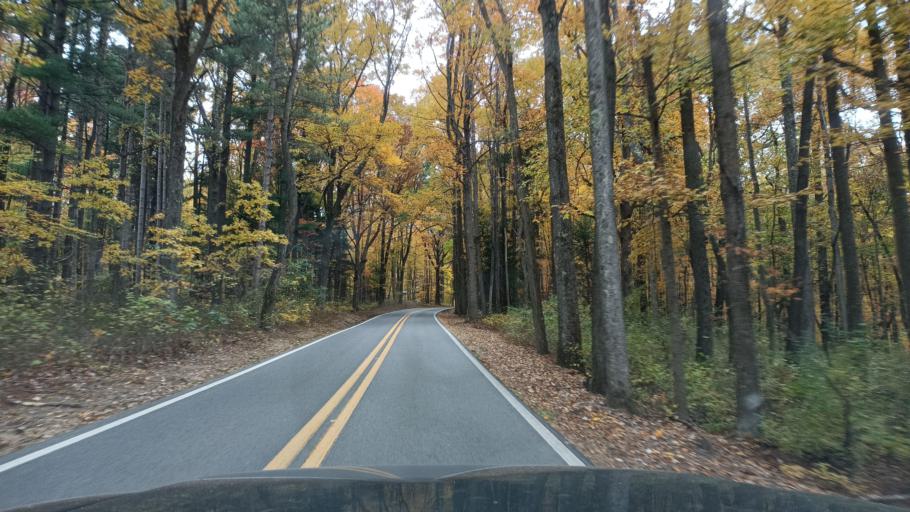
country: US
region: West Virginia
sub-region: Monongalia County
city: Cheat Lake
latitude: 39.6425
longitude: -79.7937
